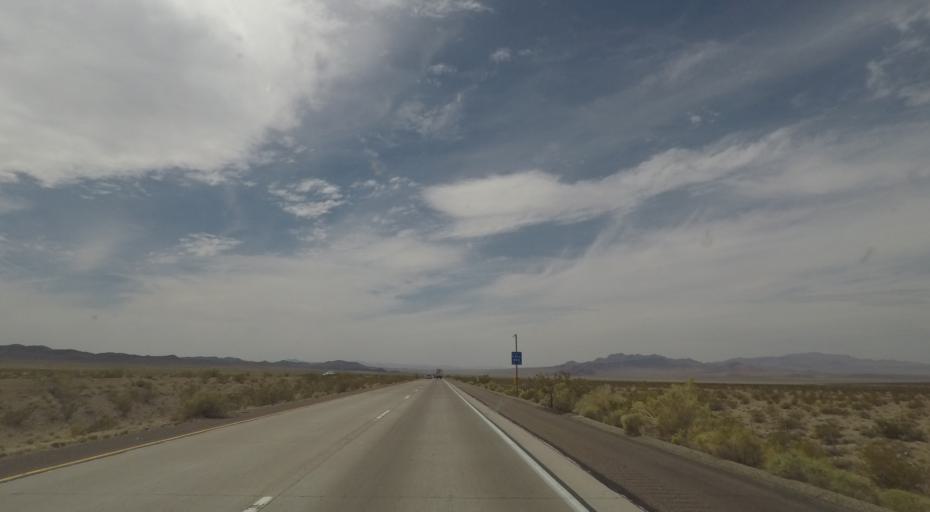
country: US
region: California
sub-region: San Bernardino County
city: Twentynine Palms
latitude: 34.7276
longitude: -116.0918
